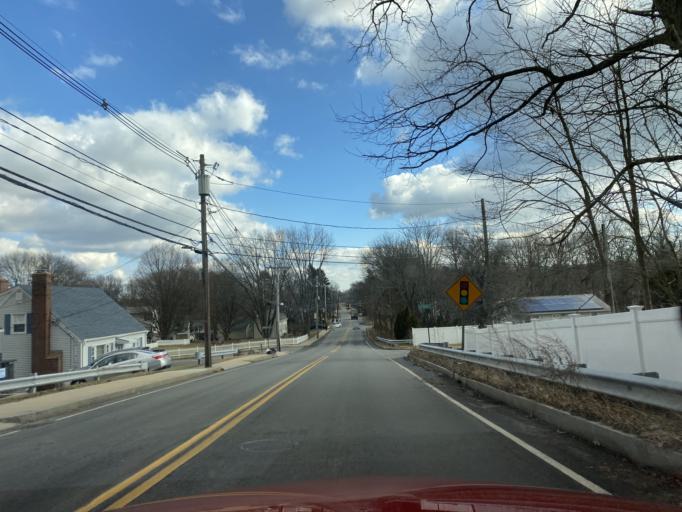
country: US
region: Massachusetts
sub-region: Middlesex County
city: Woburn
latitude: 42.4812
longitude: -71.1348
